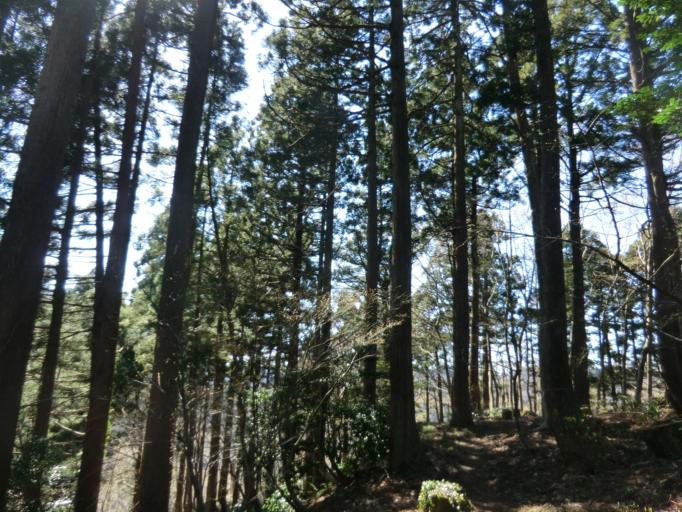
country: JP
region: Niigata
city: Nagaoka
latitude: 37.4673
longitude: 138.7423
